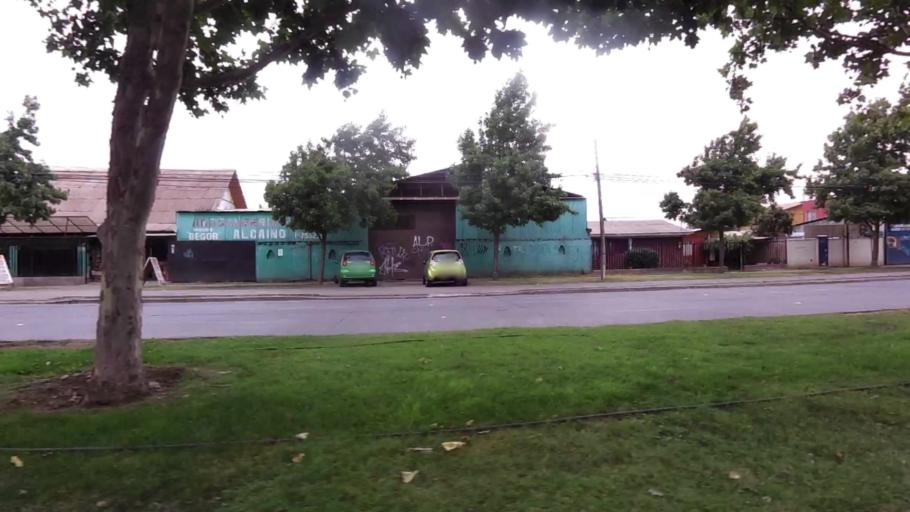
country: CL
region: O'Higgins
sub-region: Provincia de Cachapoal
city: Rancagua
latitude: -34.1505
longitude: -70.7309
